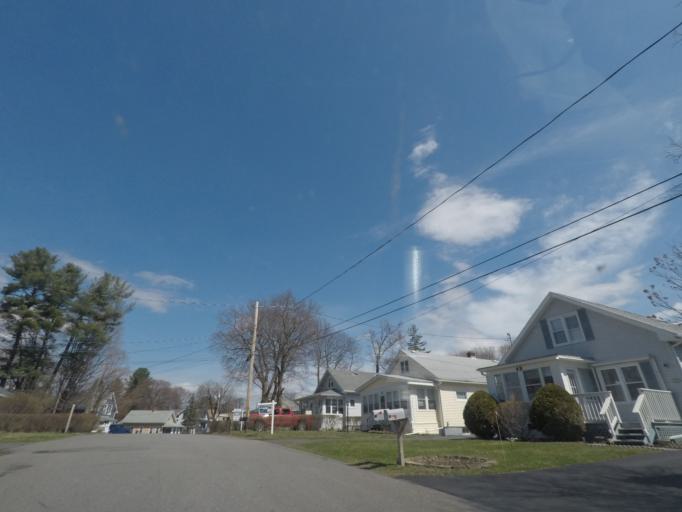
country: US
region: New York
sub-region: Rensselaer County
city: Wynantskill
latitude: 42.6986
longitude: -73.6610
